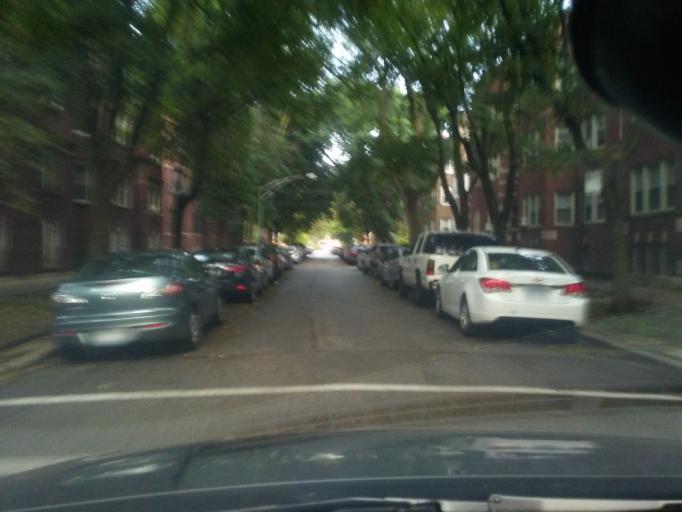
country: US
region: Illinois
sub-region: Cook County
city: Evanston
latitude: 42.0000
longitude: -87.6681
